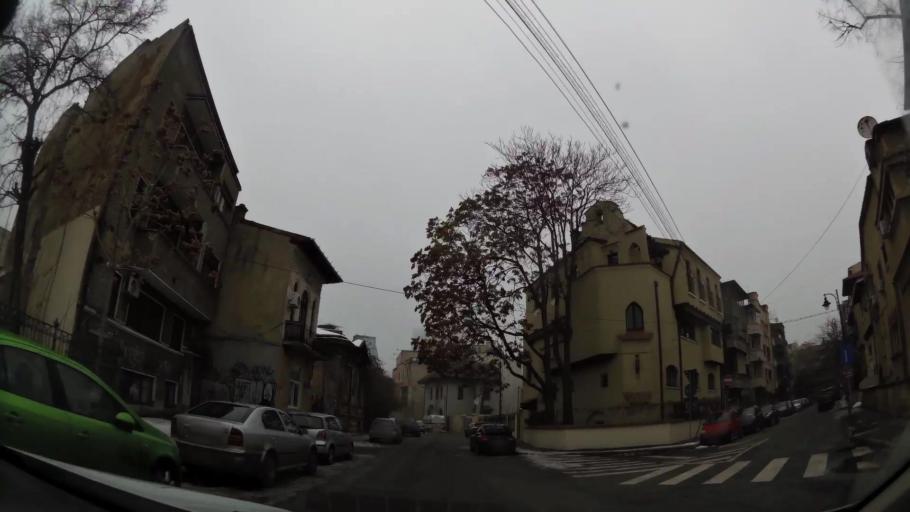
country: RO
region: Bucuresti
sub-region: Municipiul Bucuresti
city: Bucharest
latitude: 44.4447
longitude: 26.1022
